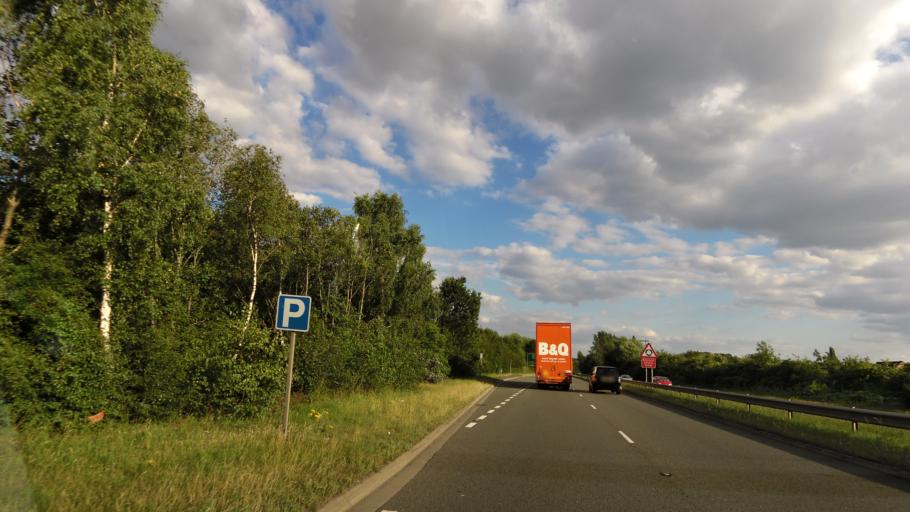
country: GB
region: England
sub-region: Nottinghamshire
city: Worksop
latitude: 53.3065
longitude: -1.1393
